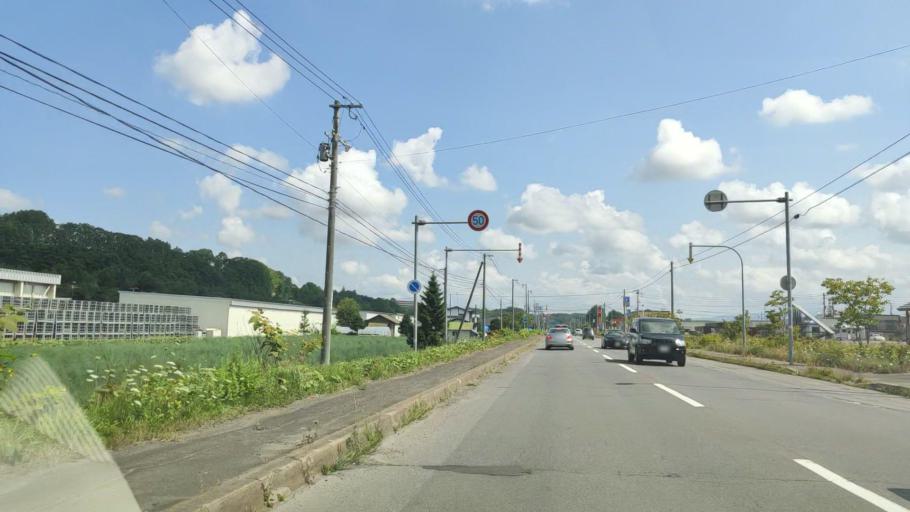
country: JP
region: Hokkaido
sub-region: Asahikawa-shi
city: Asahikawa
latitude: 43.5916
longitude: 142.4550
